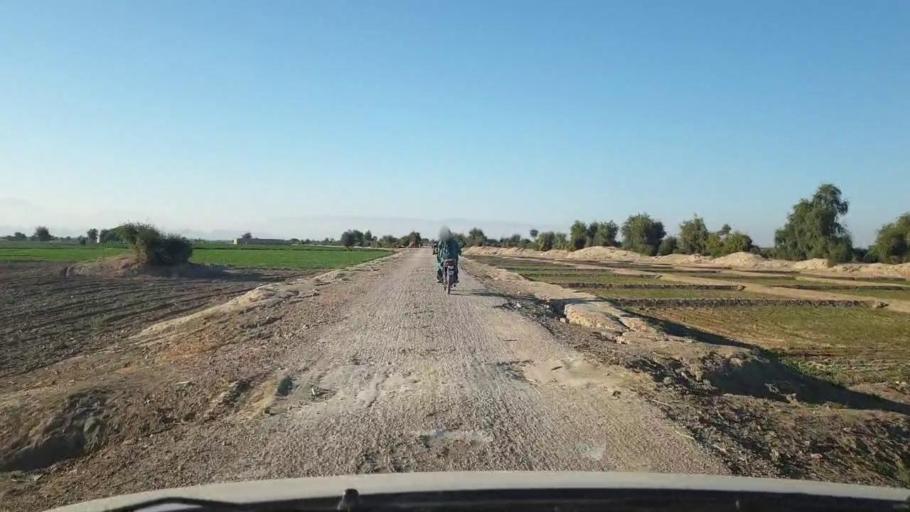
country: PK
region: Sindh
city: Johi
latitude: 26.7643
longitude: 67.4648
